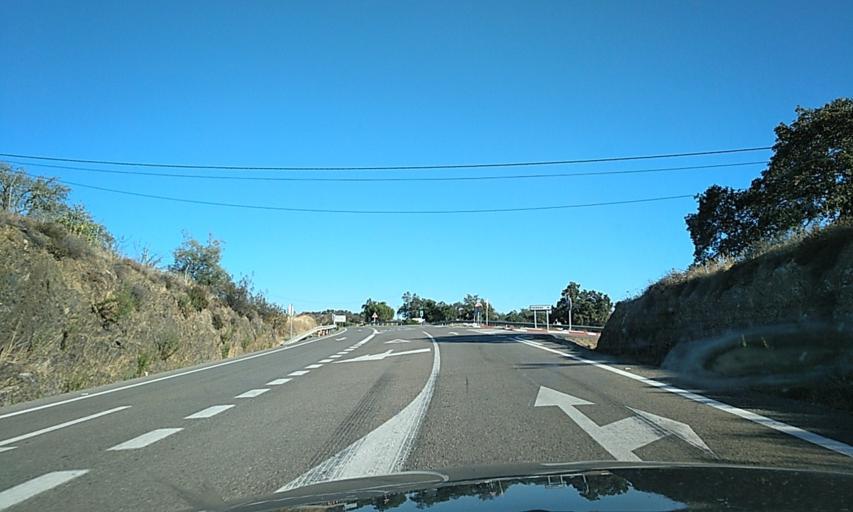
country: ES
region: Andalusia
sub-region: Provincia de Huelva
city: Santa Barbara de Casa
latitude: 37.7960
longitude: -7.1964
